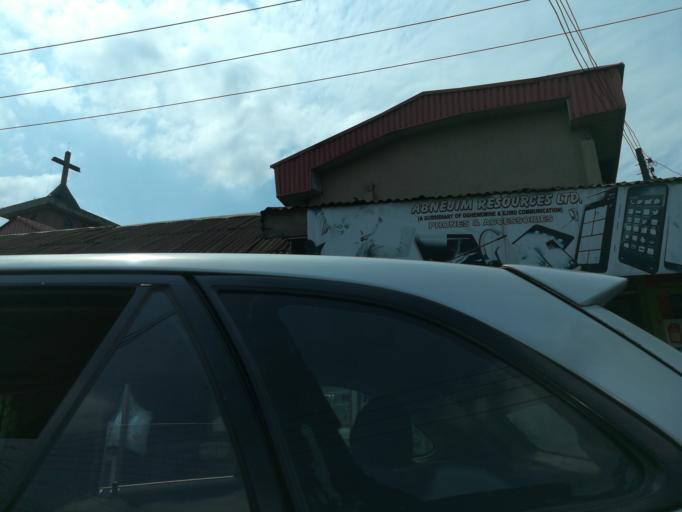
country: NG
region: Rivers
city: Port Harcourt
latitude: 4.8276
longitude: 6.9810
